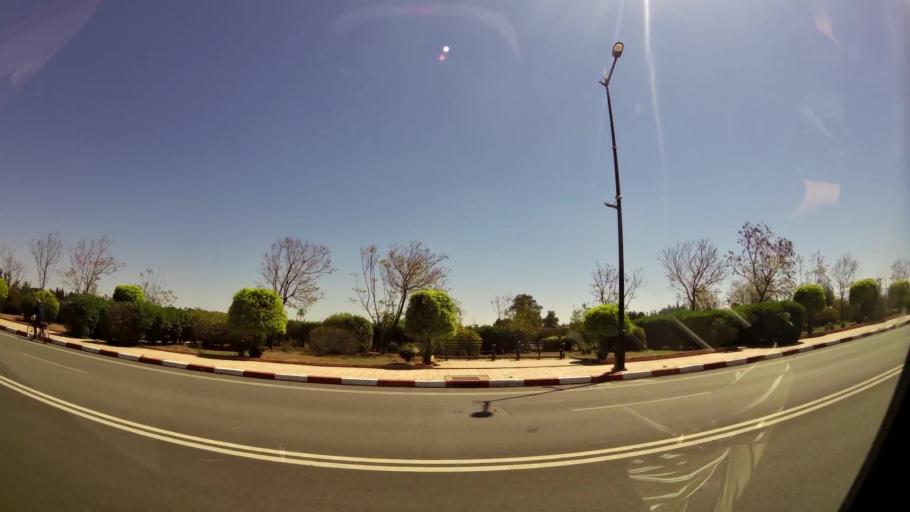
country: MA
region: Marrakech-Tensift-Al Haouz
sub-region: Marrakech
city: Marrakesh
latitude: 31.6017
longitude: -7.9879
